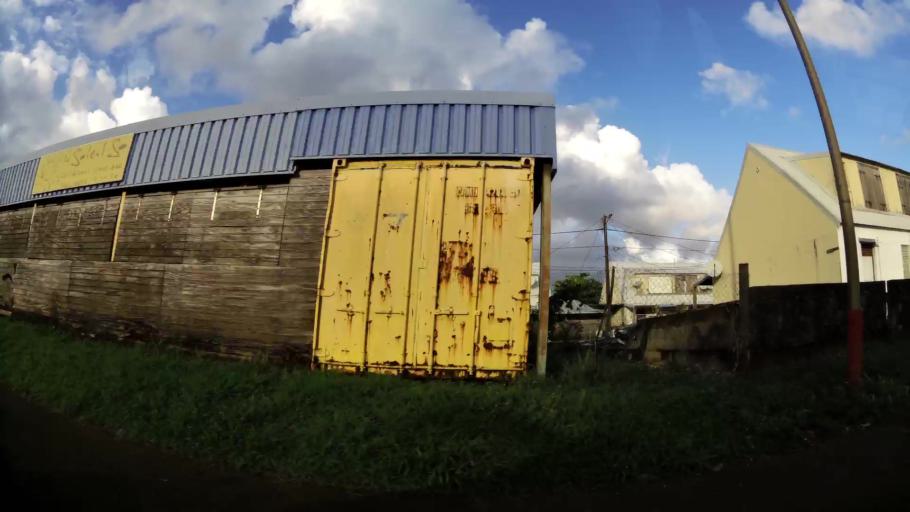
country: GP
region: Guadeloupe
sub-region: Guadeloupe
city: Petit-Bourg
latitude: 16.1315
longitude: -61.5723
